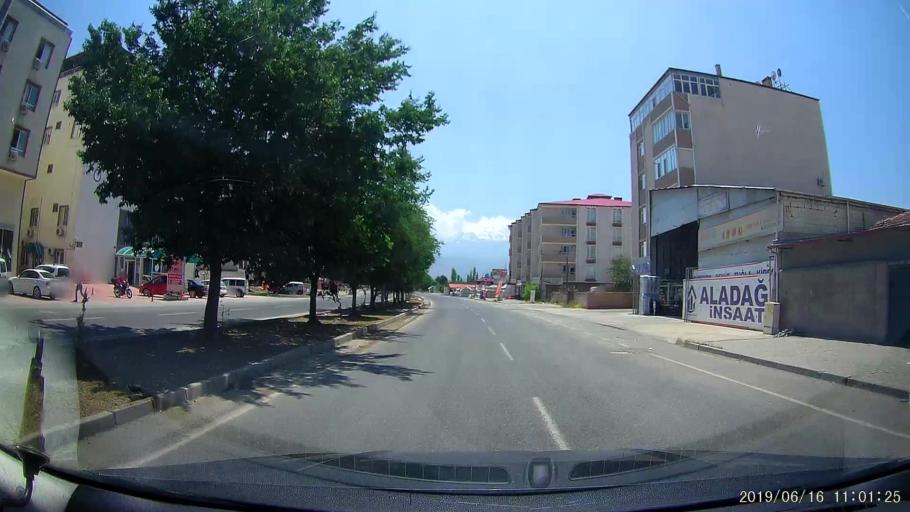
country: TR
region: Igdir
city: Igdir
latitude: 39.9150
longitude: 44.0497
